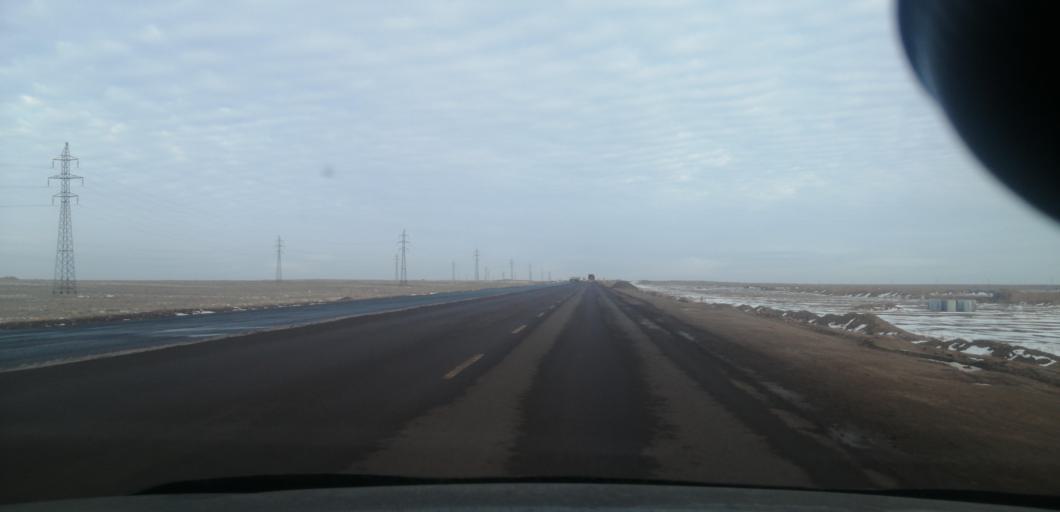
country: KZ
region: Qaraghandy
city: Balqash
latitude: 46.8010
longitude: 74.6826
